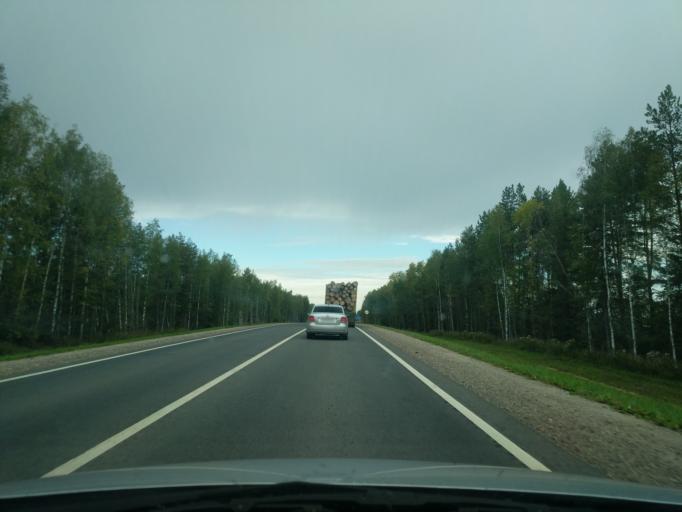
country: RU
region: Kostroma
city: Ostrovskoye
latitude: 57.8075
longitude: 42.2982
